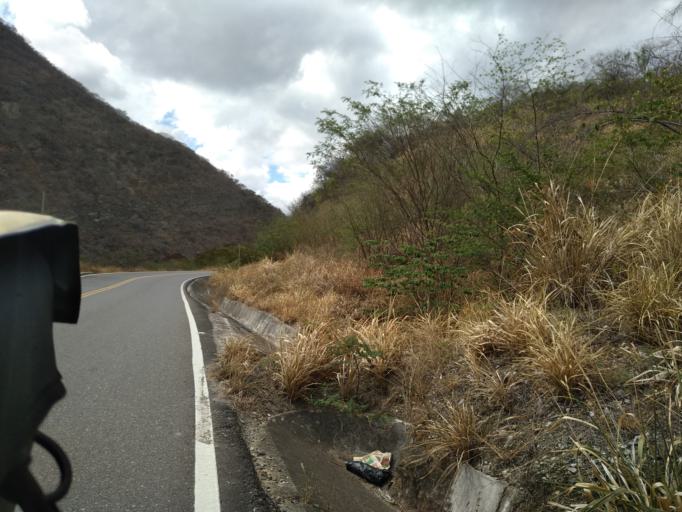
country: PE
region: Amazonas
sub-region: Utcubamba
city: Jamalca
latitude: -5.8696
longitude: -78.2160
